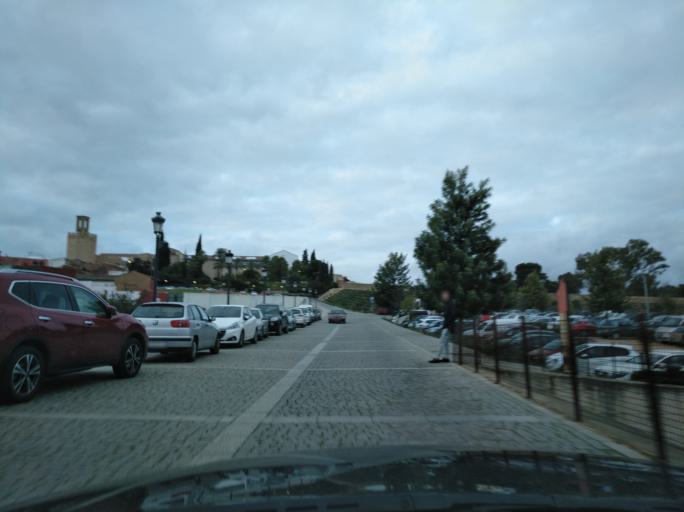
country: ES
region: Extremadura
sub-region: Provincia de Badajoz
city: Badajoz
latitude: 38.8798
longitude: -6.9654
